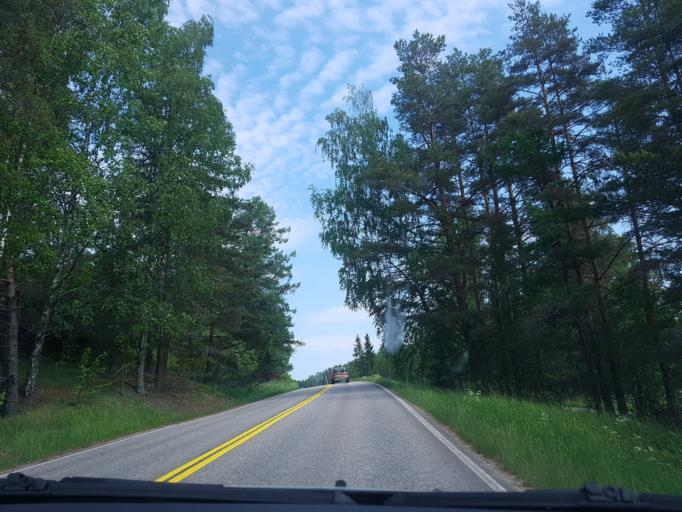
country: FI
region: Uusimaa
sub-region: Helsinki
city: Vihti
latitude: 60.3169
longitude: 24.4035
